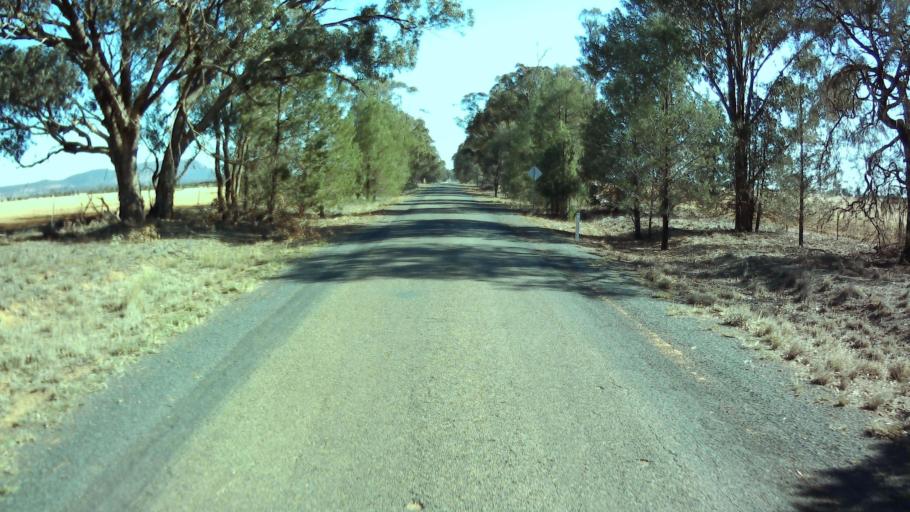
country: AU
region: New South Wales
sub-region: Weddin
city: Grenfell
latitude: -33.8052
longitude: 147.9550
